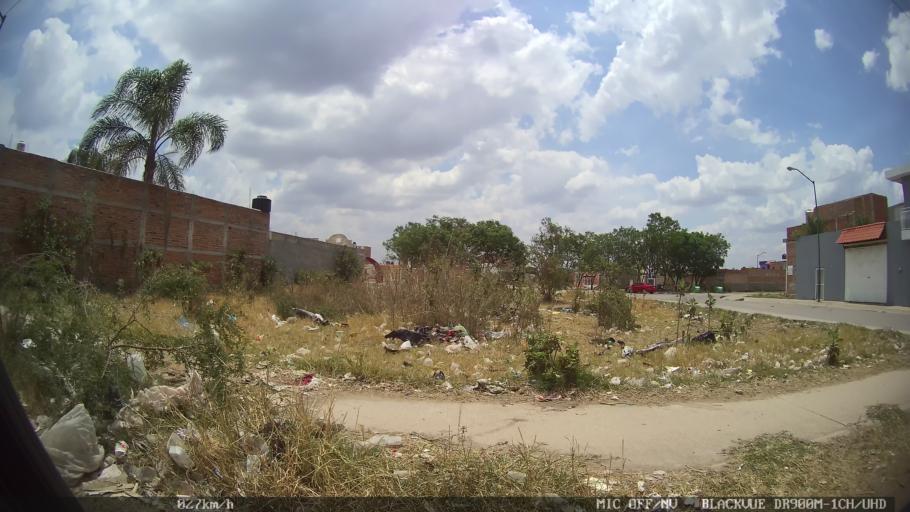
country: MX
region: Jalisco
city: Tonala
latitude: 20.6642
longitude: -103.2264
